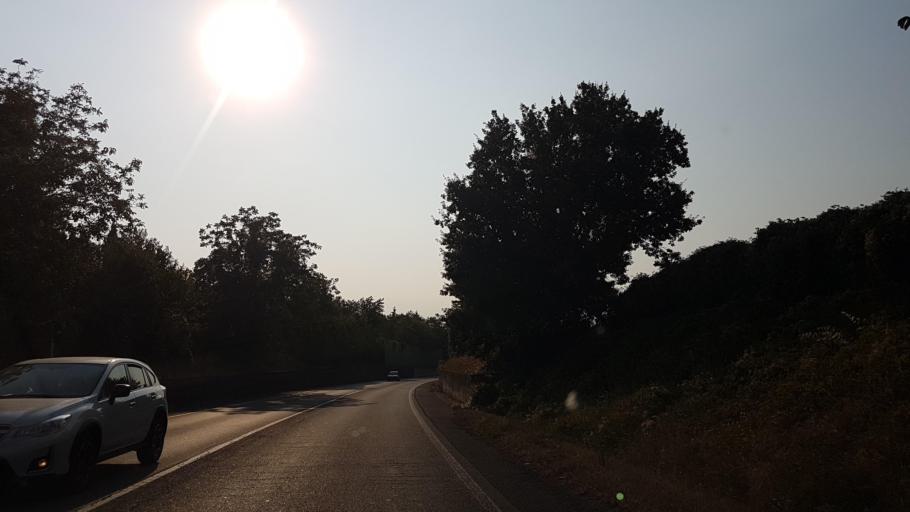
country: IT
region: Emilia-Romagna
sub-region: Provincia di Parma
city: Collecchio
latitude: 44.7574
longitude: 10.2183
